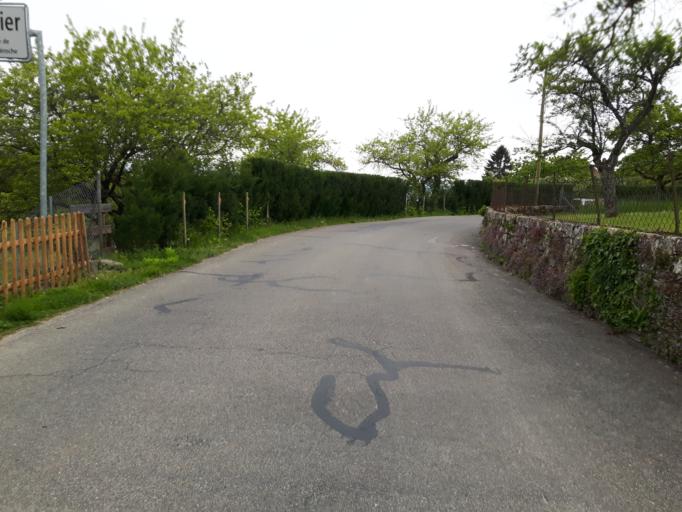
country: CH
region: Neuchatel
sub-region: Boudry District
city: Gorgier
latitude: 46.9049
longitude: 6.7820
